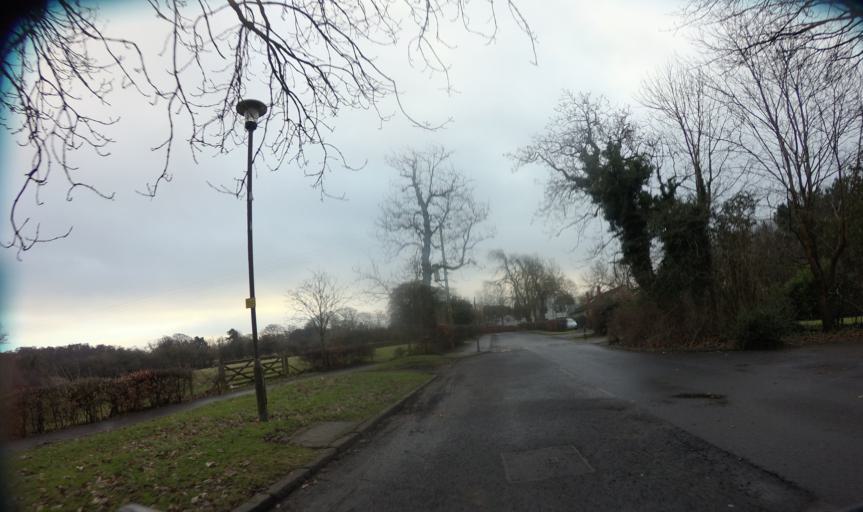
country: GB
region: Scotland
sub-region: West Lothian
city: Livingston
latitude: 55.8686
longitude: -3.5271
